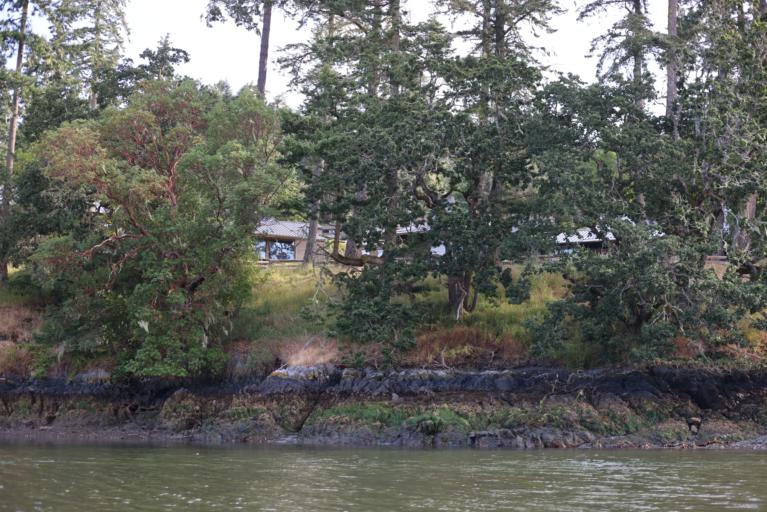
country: CA
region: British Columbia
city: Metchosin
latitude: 48.3460
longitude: -123.5644
